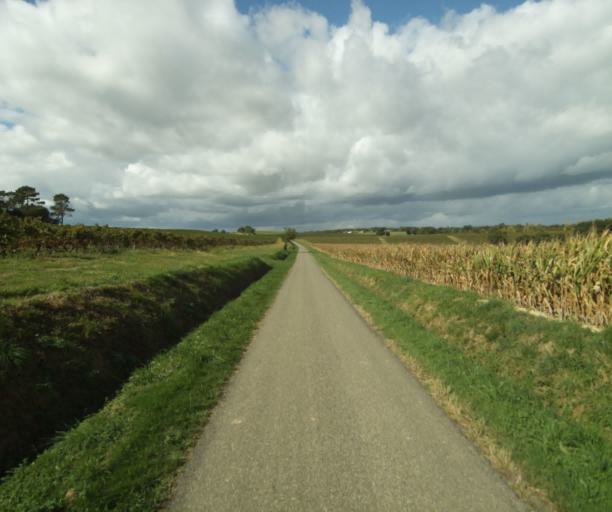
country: FR
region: Midi-Pyrenees
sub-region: Departement du Gers
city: Nogaro
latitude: 43.8460
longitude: -0.0288
